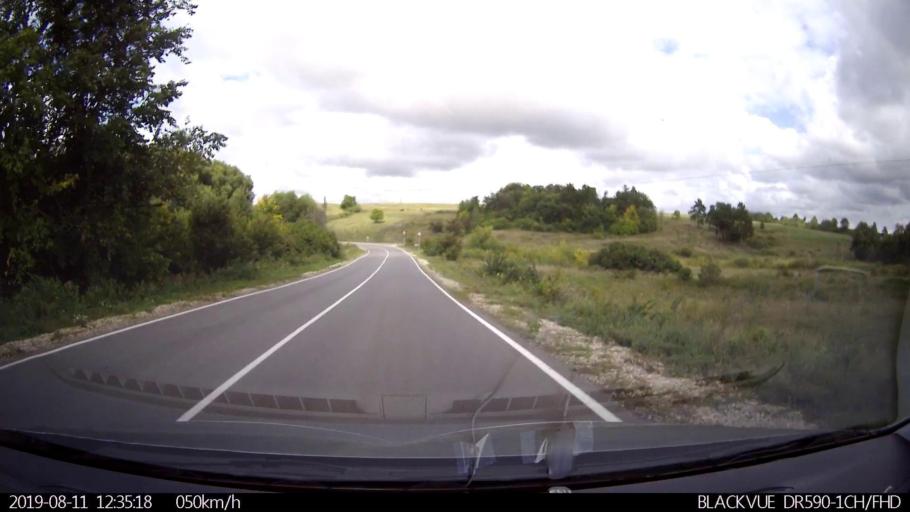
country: RU
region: Ulyanovsk
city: Ignatovka
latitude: 53.8236
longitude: 47.8341
